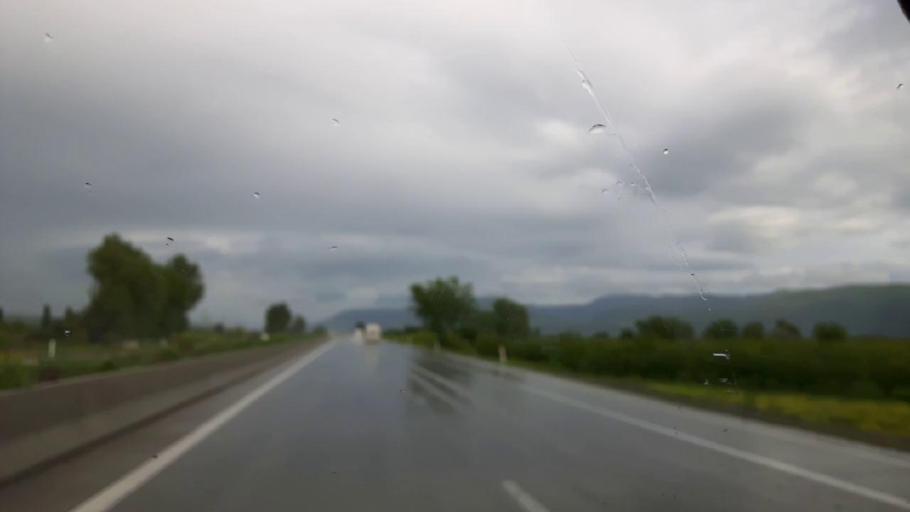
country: GE
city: Agara
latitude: 42.0373
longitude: 43.9369
